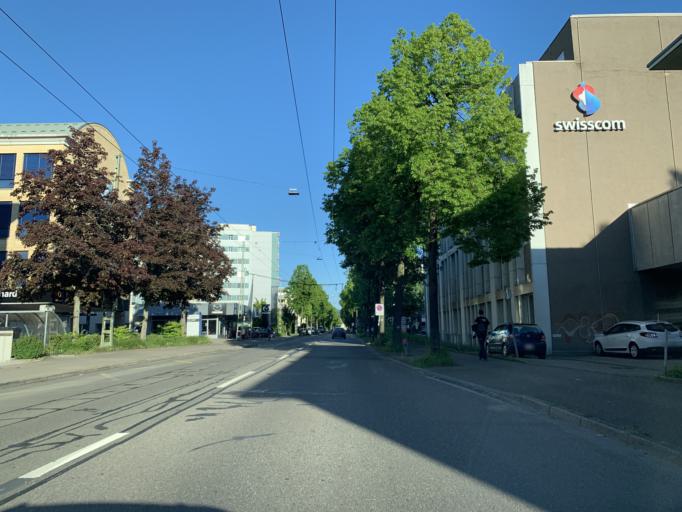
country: CH
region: Zurich
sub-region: Bezirk Winterthur
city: Mattenbach (Kreis 7) / Endliker
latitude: 47.4896
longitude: 8.7498
